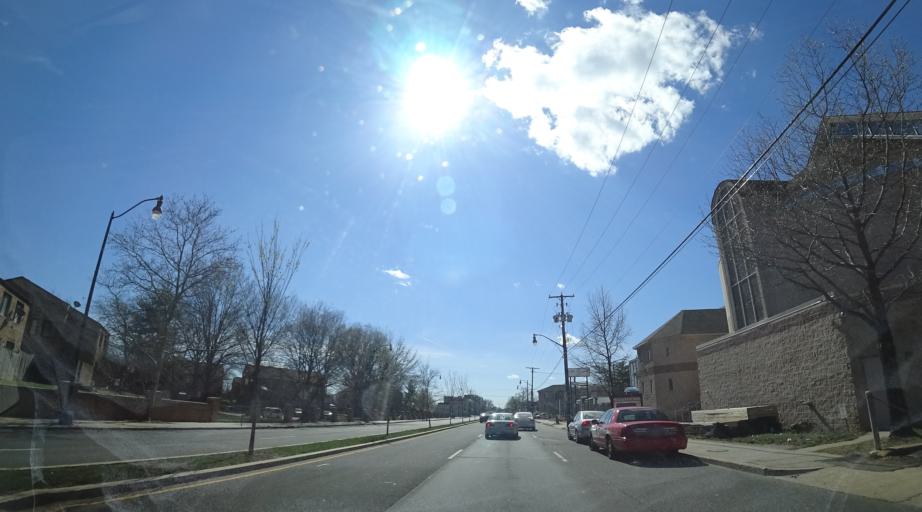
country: US
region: Maryland
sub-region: Prince George's County
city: Mount Rainier
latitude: 38.9267
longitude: -76.9636
